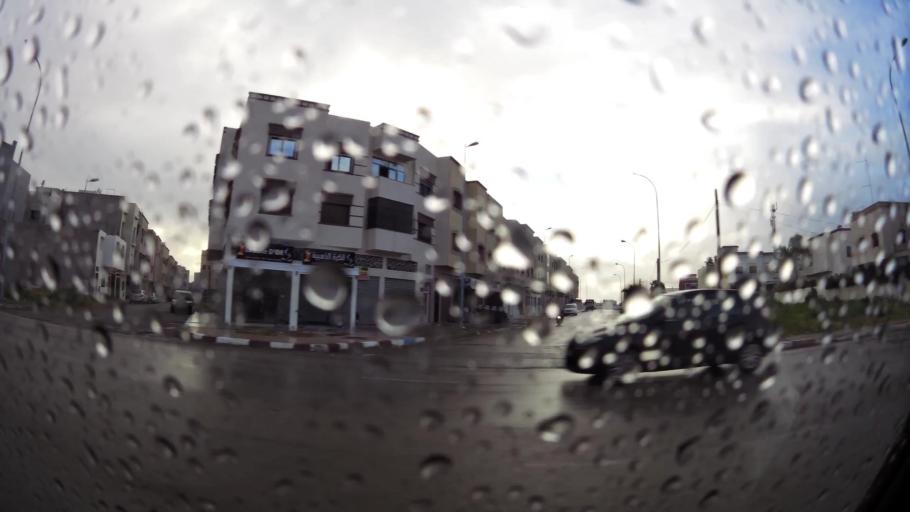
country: MA
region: Doukkala-Abda
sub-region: El-Jadida
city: El Jadida
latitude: 33.2434
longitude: -8.5142
